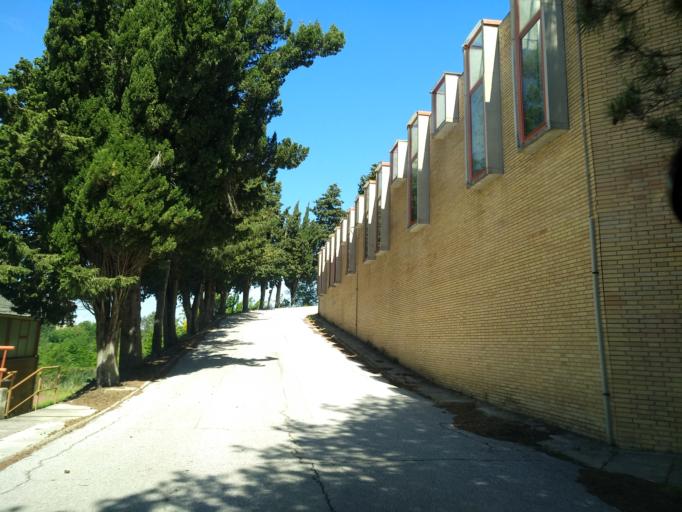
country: IT
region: The Marches
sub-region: Provincia di Pesaro e Urbino
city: Urbino
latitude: 43.7358
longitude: 12.6289
